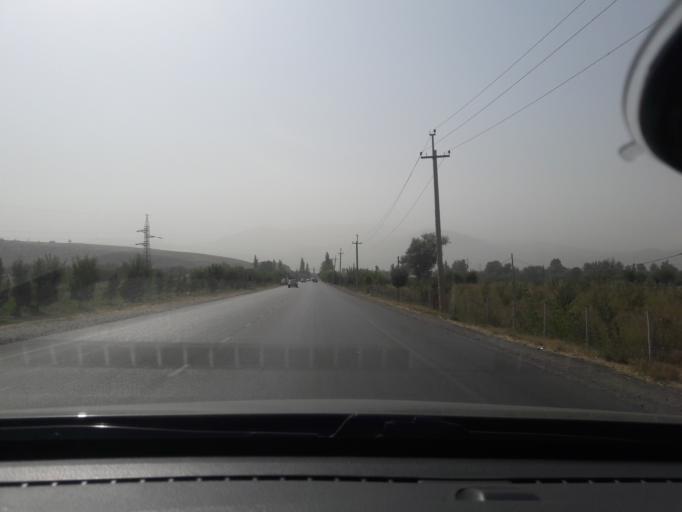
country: TJ
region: Republican Subordination
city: Vahdat
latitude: 38.5285
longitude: 69.0264
